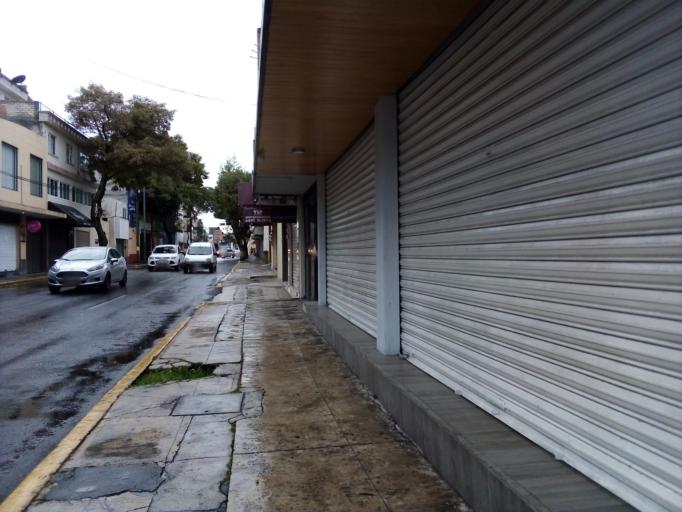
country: MX
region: Mexico
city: Toluca
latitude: 19.2873
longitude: -99.6577
